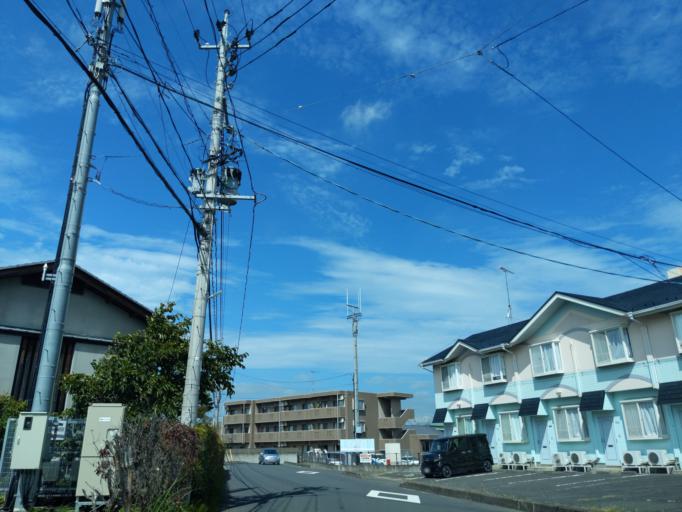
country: JP
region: Fukushima
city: Koriyama
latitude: 37.4225
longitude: 140.3796
